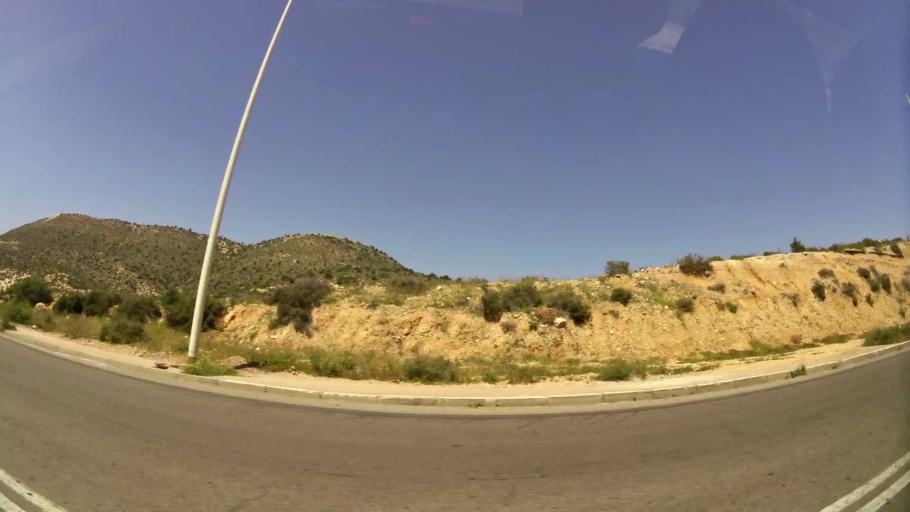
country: MA
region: Souss-Massa-Draa
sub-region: Agadir-Ida-ou-Tnan
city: Agadir
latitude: 30.4300
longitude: -9.6117
